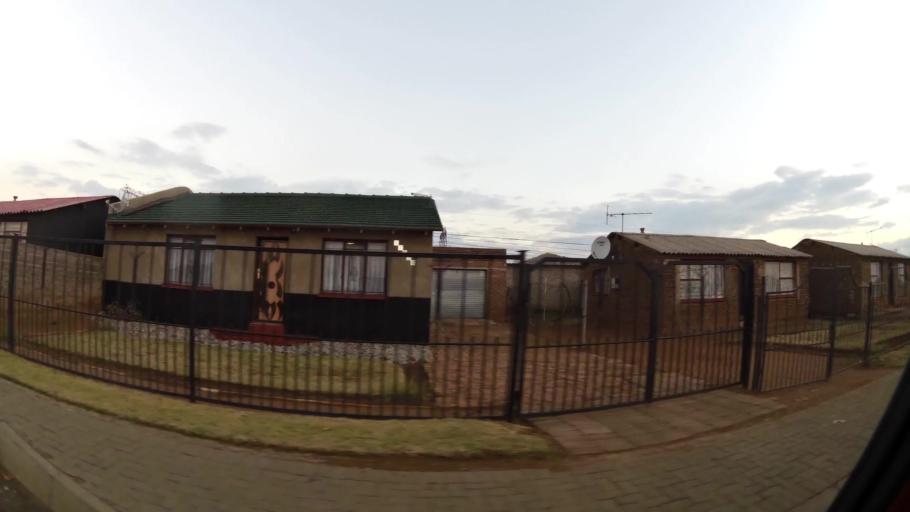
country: ZA
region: Gauteng
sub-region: City of Johannesburg Metropolitan Municipality
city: Orange Farm
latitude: -26.5579
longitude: 27.8642
